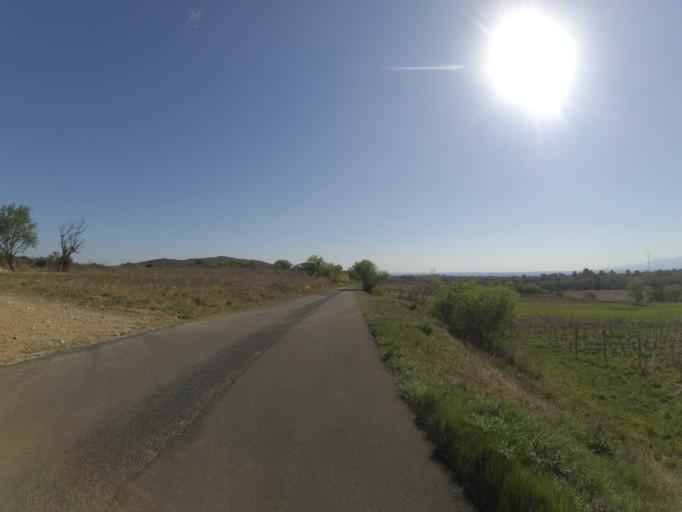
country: FR
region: Languedoc-Roussillon
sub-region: Departement des Pyrenees-Orientales
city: Estagel
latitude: 42.7580
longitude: 2.7455
